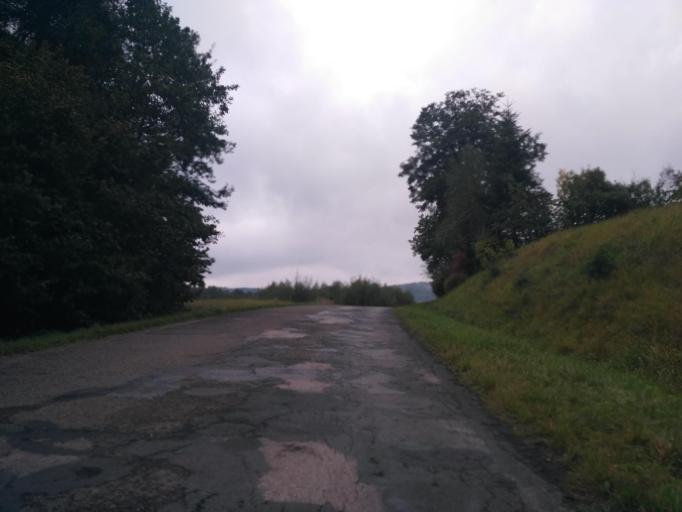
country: PL
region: Subcarpathian Voivodeship
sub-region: Powiat debicki
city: Brzostek
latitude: 49.9251
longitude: 21.4616
